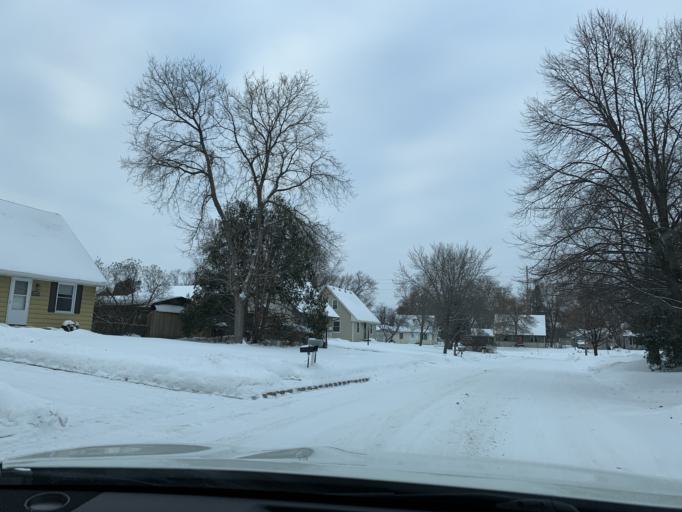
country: US
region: Minnesota
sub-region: Anoka County
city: Coon Rapids
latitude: 45.1665
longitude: -93.2873
